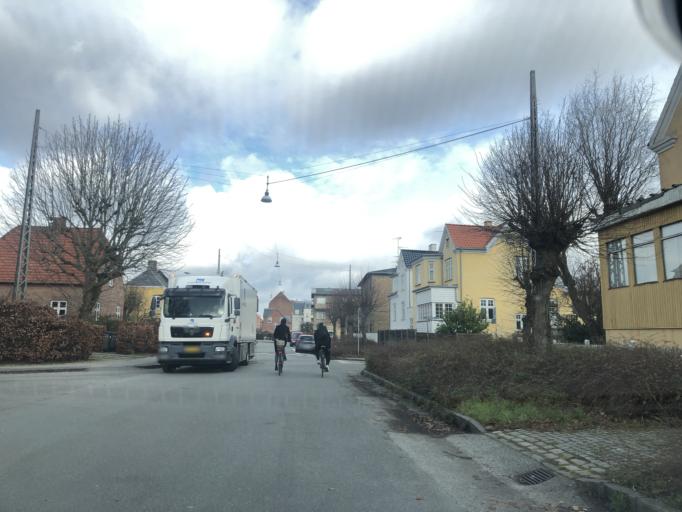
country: DK
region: Capital Region
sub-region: Tarnby Kommune
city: Tarnby
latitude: 55.6490
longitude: 12.6178
